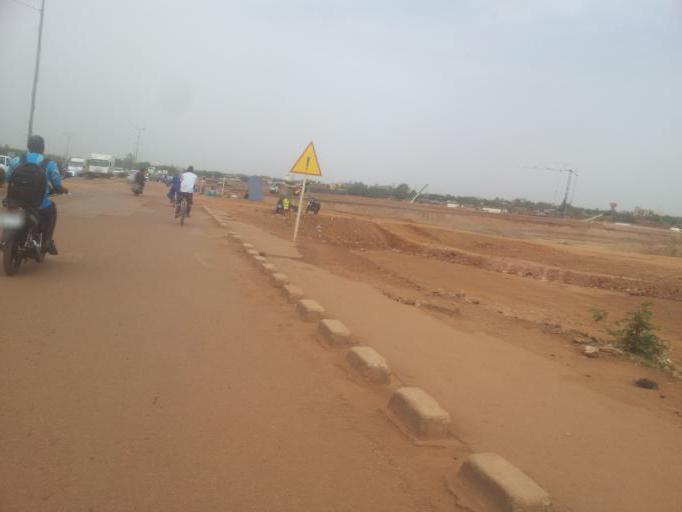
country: BF
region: Centre
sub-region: Kadiogo Province
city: Ouagadougou
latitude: 12.3858
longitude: -1.5584
